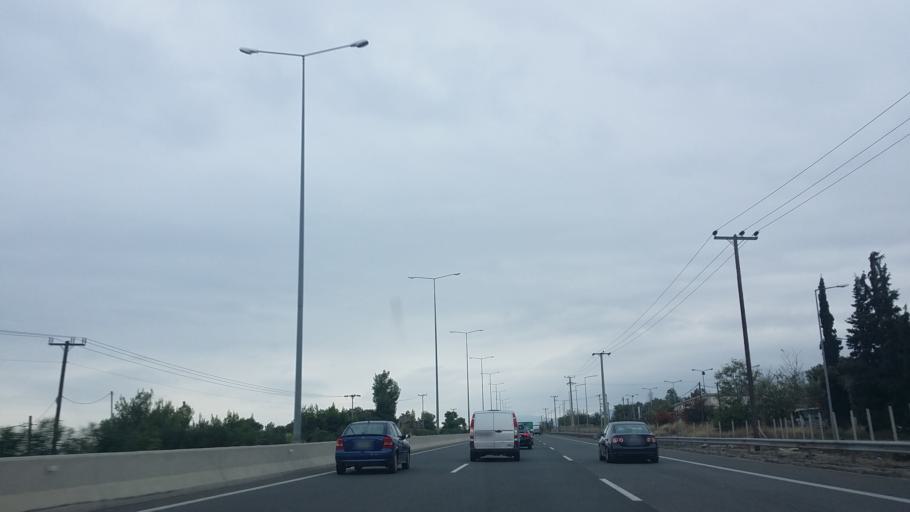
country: GR
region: Central Greece
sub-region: Nomos Voiotias
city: Oinofyta
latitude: 38.2967
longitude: 23.6655
